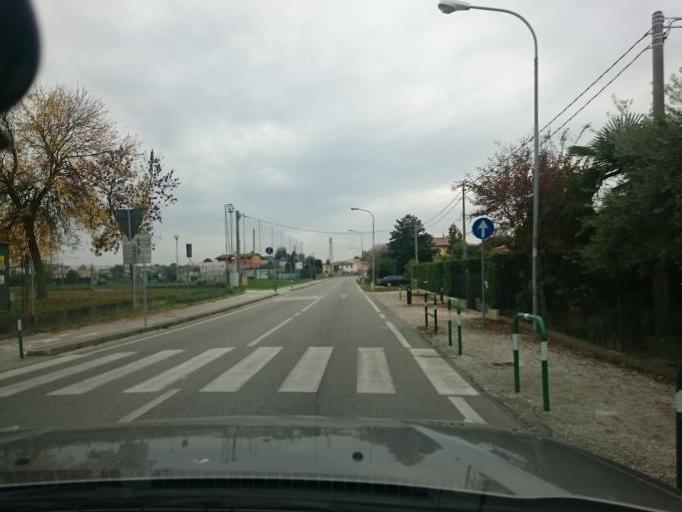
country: IT
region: Veneto
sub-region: Provincia di Padova
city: Arzergrande
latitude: 45.2770
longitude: 12.0284
